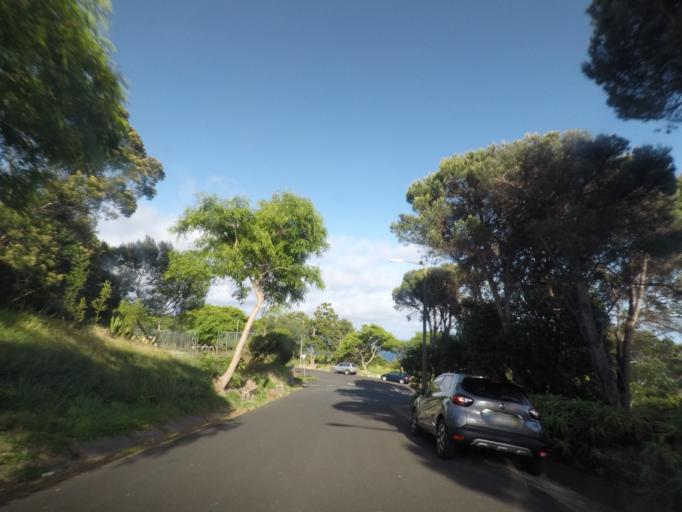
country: PT
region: Madeira
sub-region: Machico
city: Machico
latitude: 32.7107
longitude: -16.7671
